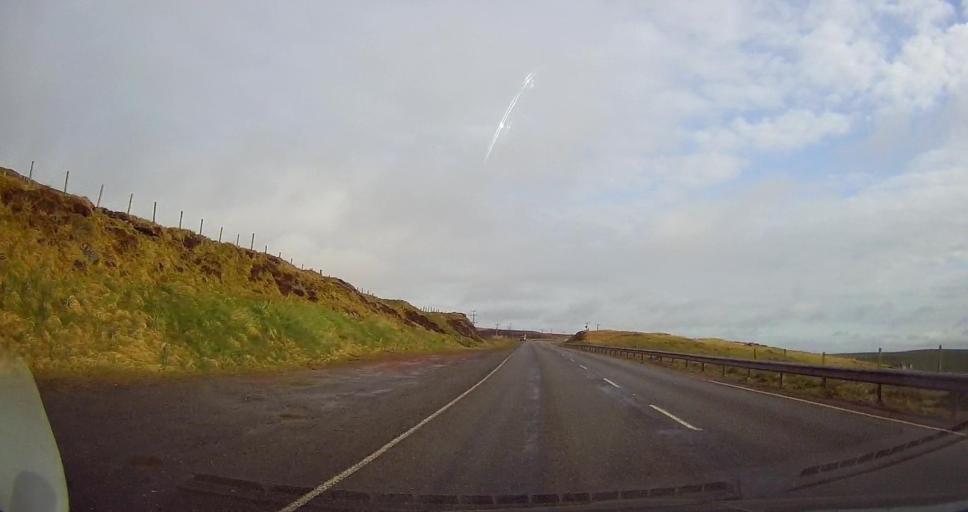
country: GB
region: Scotland
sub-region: Shetland Islands
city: Lerwick
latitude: 60.1105
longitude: -1.2191
